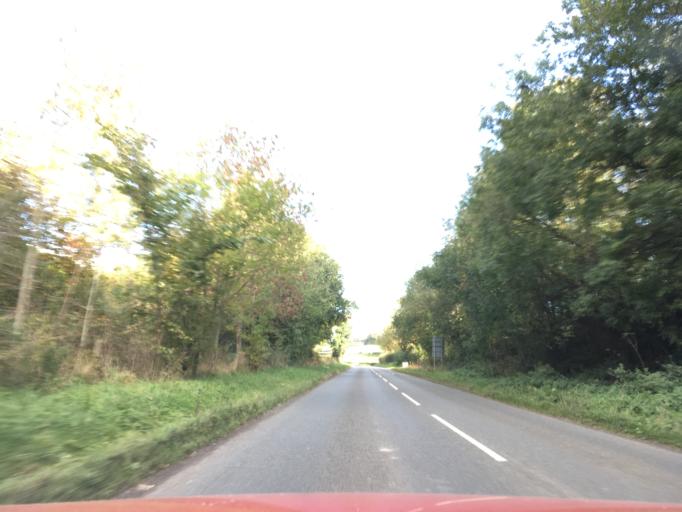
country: GB
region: Wales
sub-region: Sir Powys
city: Hay
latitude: 52.0488
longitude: -3.1871
